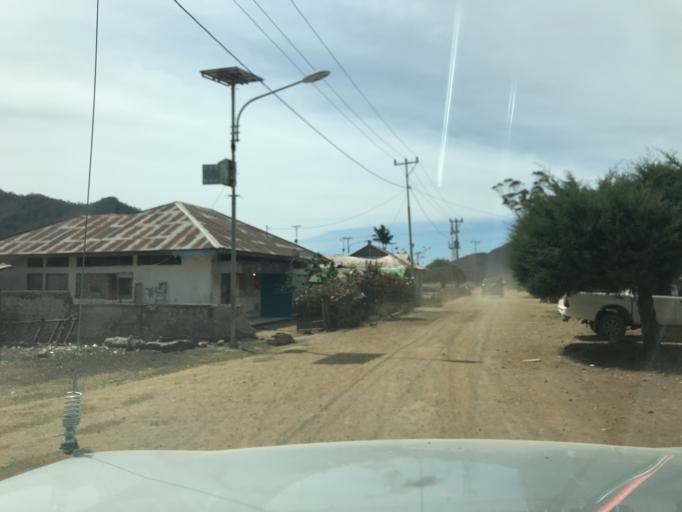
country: TL
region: Ainaro
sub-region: Ainaro
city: Ainaro
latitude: -8.9005
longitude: 125.5197
